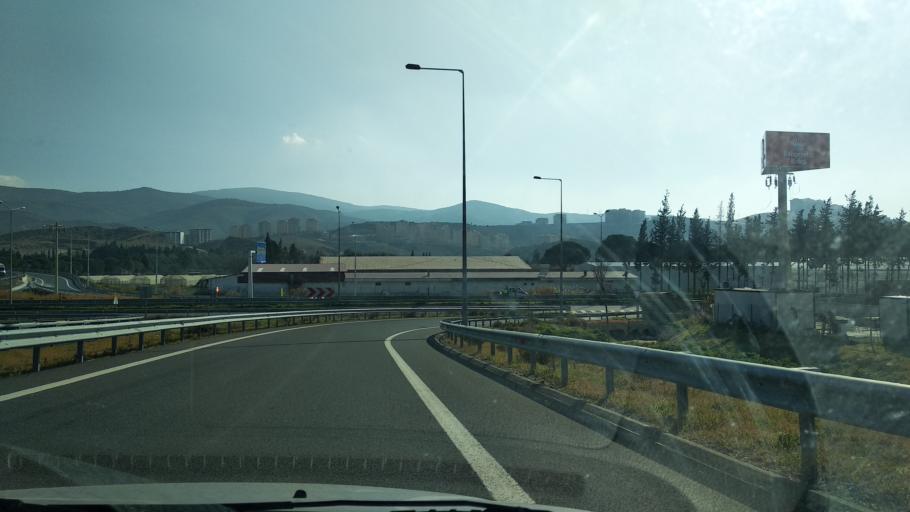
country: TR
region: Izmir
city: Menemen
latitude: 38.5702
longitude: 27.0548
